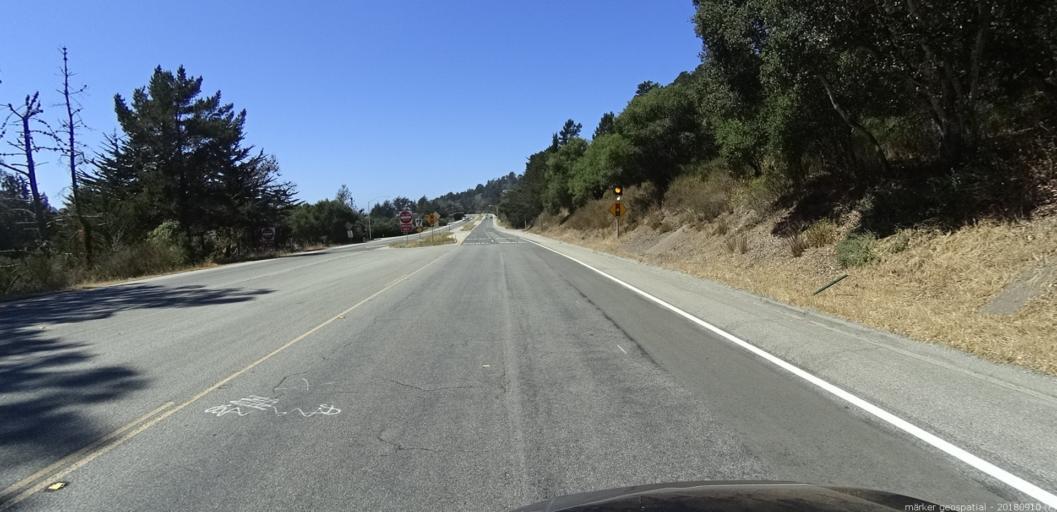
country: US
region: California
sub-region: Monterey County
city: Carmel-by-the-Sea
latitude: 36.5409
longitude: -121.8763
